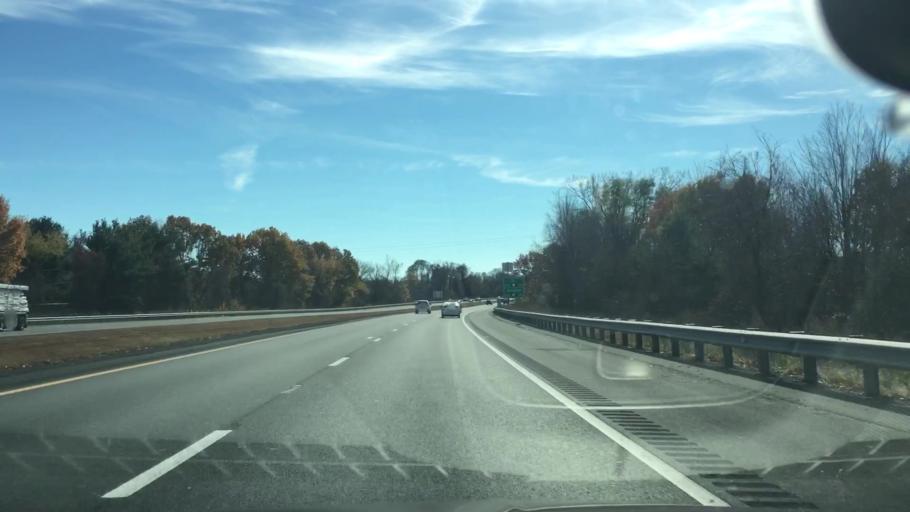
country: US
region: Massachusetts
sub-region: Hampshire County
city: Northampton
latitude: 42.3246
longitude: -72.6159
